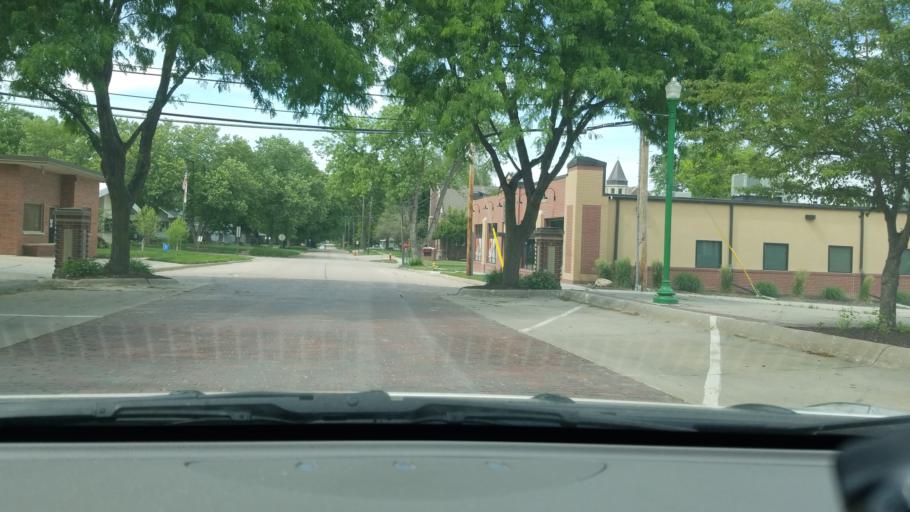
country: US
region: Nebraska
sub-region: Saunders County
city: Ashland
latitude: 41.0394
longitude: -96.3696
